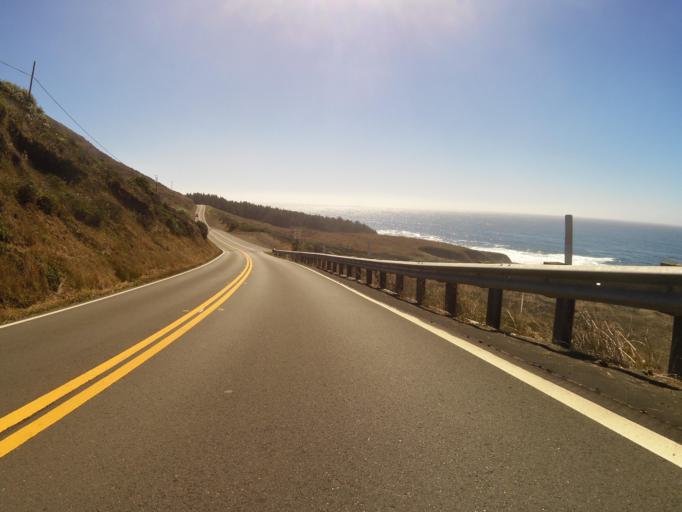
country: US
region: California
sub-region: Mendocino County
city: Fort Bragg
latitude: 39.6071
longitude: -123.7838
